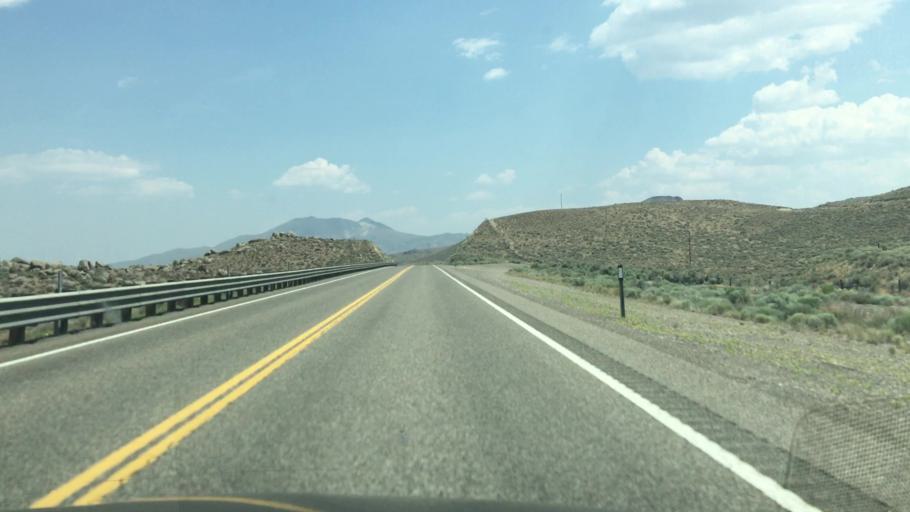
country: US
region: Nevada
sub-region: Elko County
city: Jackpot
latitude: 41.7390
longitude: -114.7825
